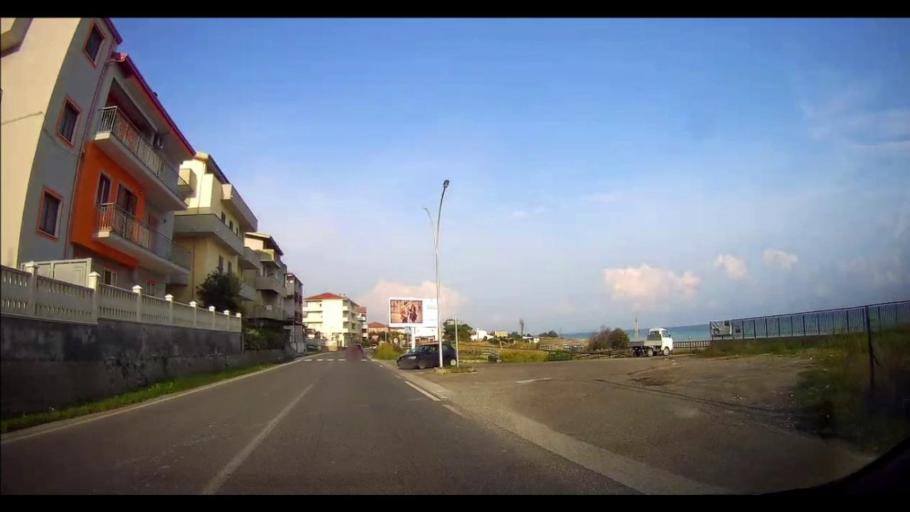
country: IT
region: Calabria
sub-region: Provincia di Cosenza
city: Cariati
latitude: 39.5087
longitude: 16.9326
